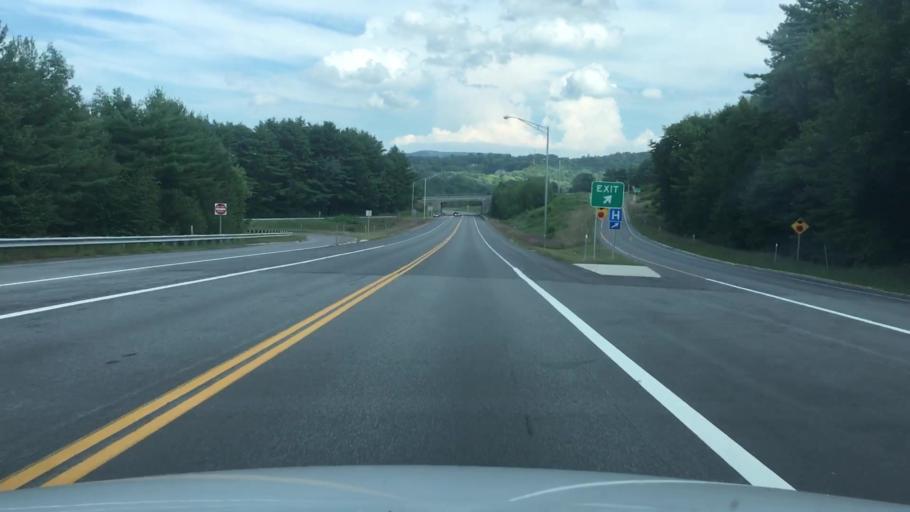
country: US
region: New Hampshire
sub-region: Belknap County
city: Laconia
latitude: 43.5126
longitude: -71.4634
